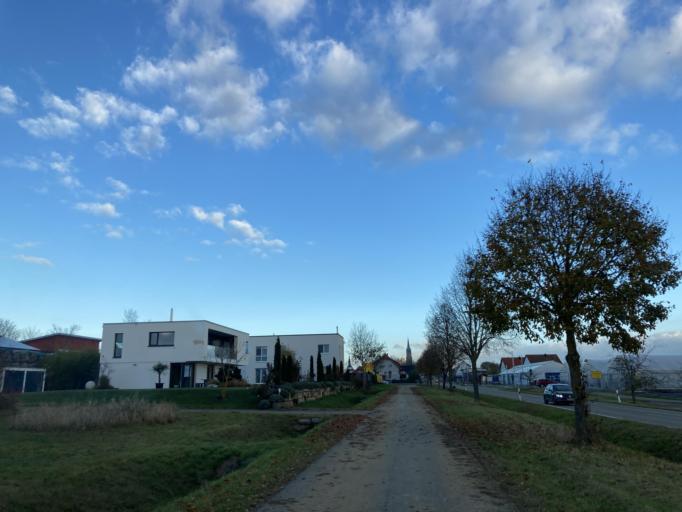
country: DE
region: Baden-Wuerttemberg
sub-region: Tuebingen Region
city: Haigerloch
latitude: 48.4322
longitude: 8.8041
